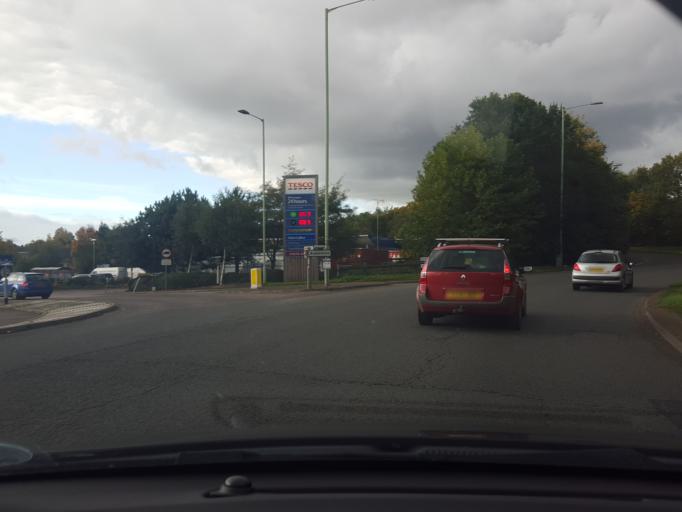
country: GB
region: England
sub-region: Suffolk
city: Bury St Edmunds
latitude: 52.2546
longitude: 0.7175
